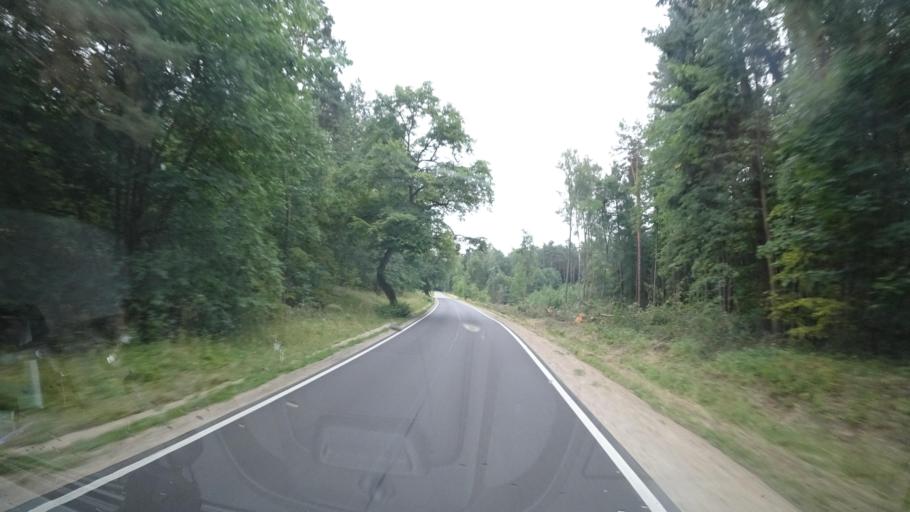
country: PL
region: Warmian-Masurian Voivodeship
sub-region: Powiat gizycki
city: Ryn
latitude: 53.8869
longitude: 21.5757
